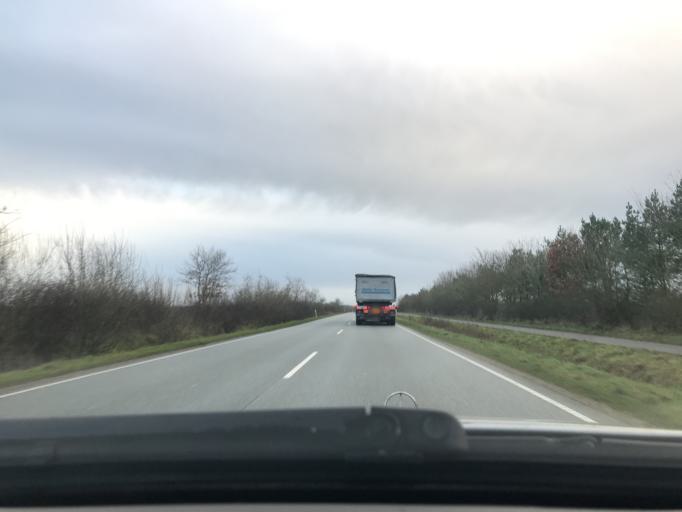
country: DK
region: South Denmark
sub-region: Tonder Kommune
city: Sherrebek
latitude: 55.1855
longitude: 8.7358
